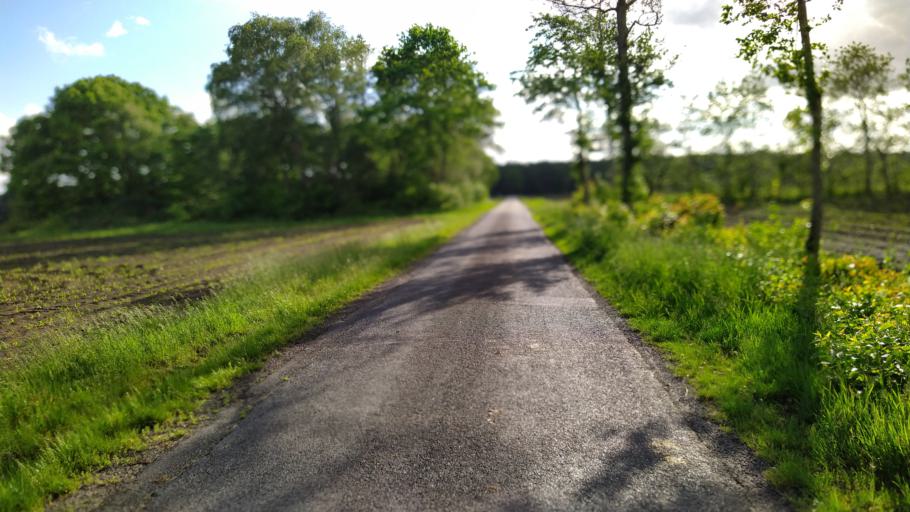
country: DE
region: Lower Saxony
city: Farven
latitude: 53.4425
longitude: 9.3076
